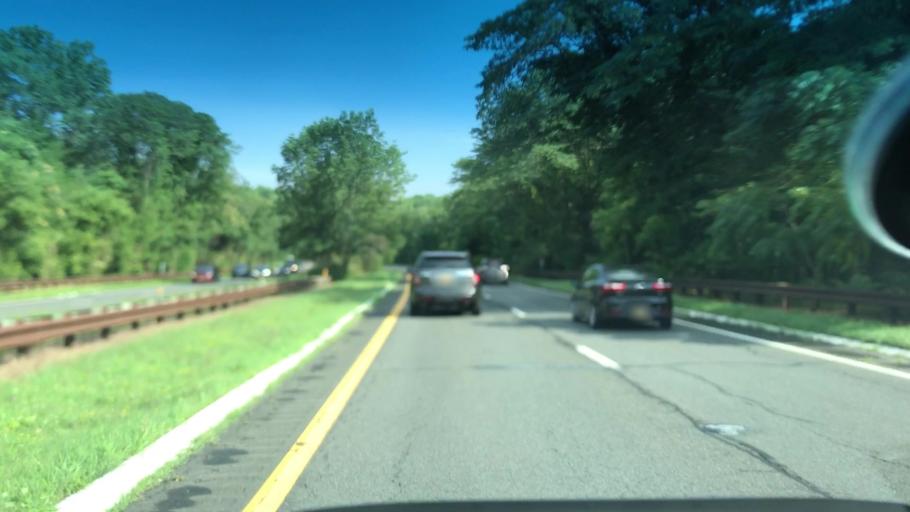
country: US
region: New York
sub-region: Rockland County
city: Sparkill
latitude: 41.0212
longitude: -73.9335
